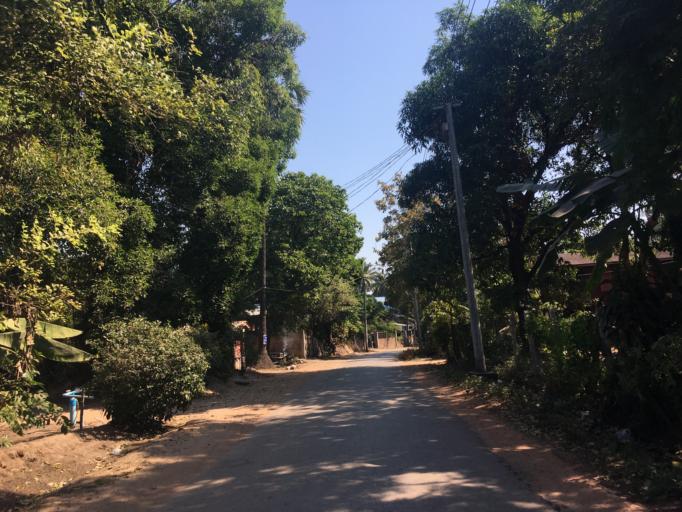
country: MM
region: Mon
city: Mawlamyine
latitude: 16.4322
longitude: 97.7012
